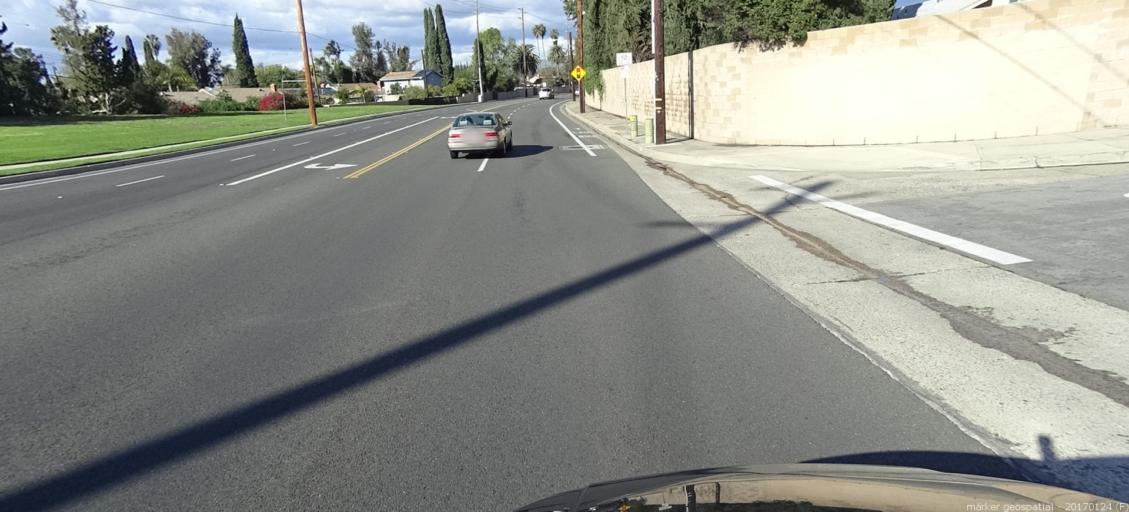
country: US
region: California
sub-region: Orange County
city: Laguna Hills
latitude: 33.6103
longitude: -117.6969
